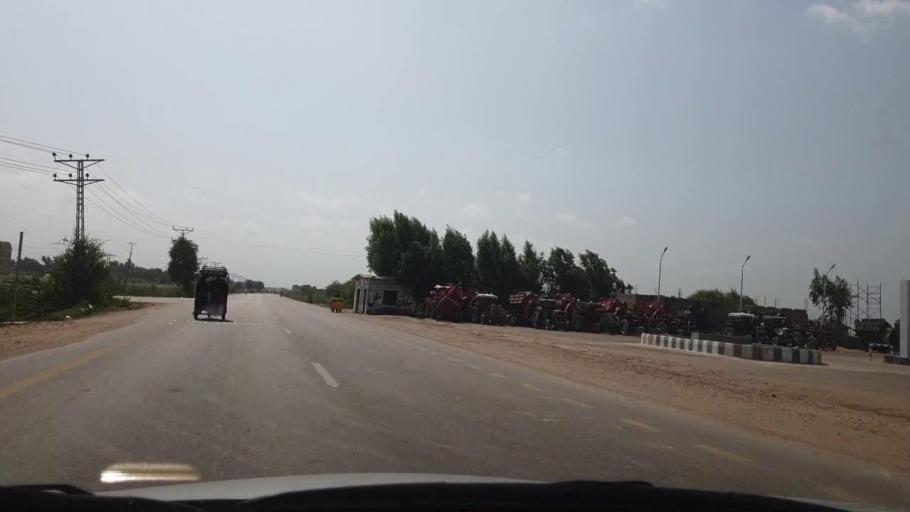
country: PK
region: Sindh
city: Matli
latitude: 24.9968
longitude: 68.6540
